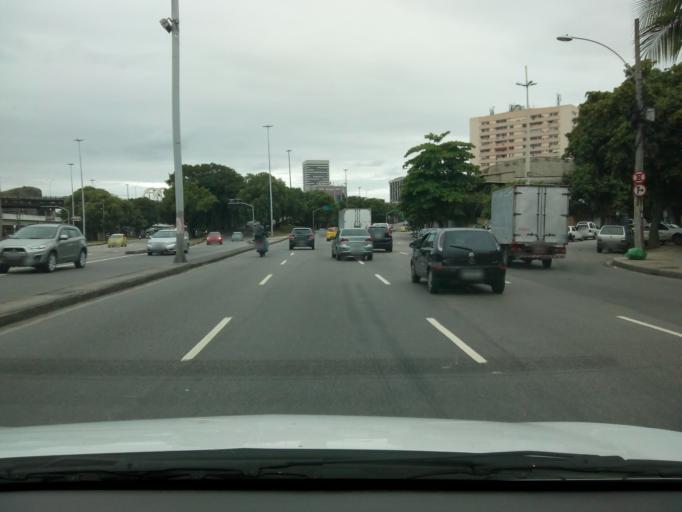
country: BR
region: Rio de Janeiro
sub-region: Rio De Janeiro
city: Rio de Janeiro
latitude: -22.9110
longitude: -43.2133
